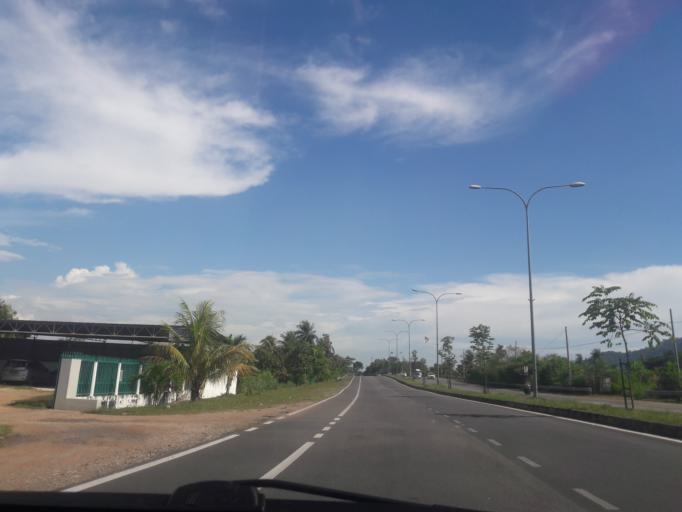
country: MY
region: Kedah
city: Sungai Petani
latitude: 5.6236
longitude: 100.4641
